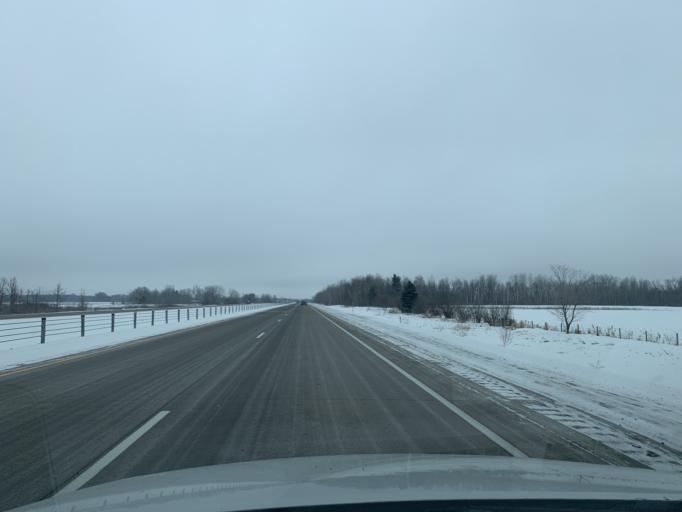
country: US
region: Minnesota
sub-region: Chisago County
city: Rush City
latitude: 45.7086
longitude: -92.9925
